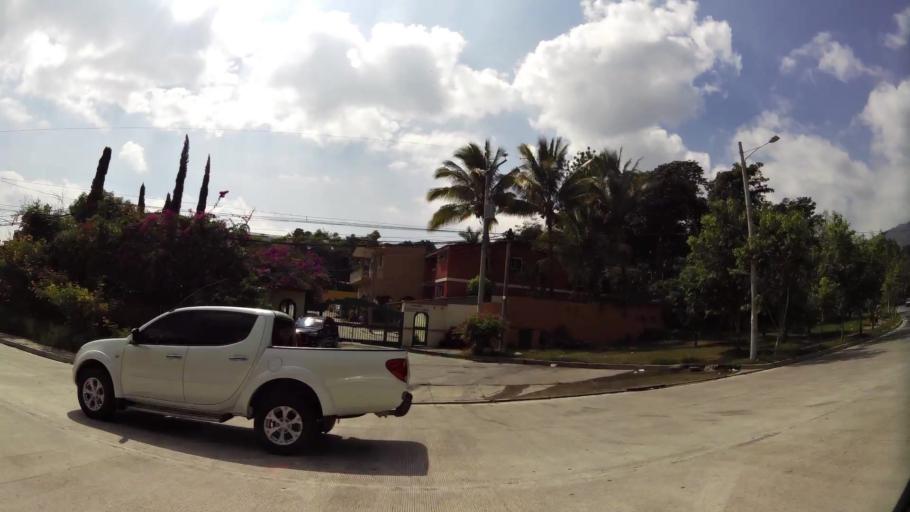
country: SV
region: San Salvador
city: Mejicanos
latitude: 13.7137
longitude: -89.2383
